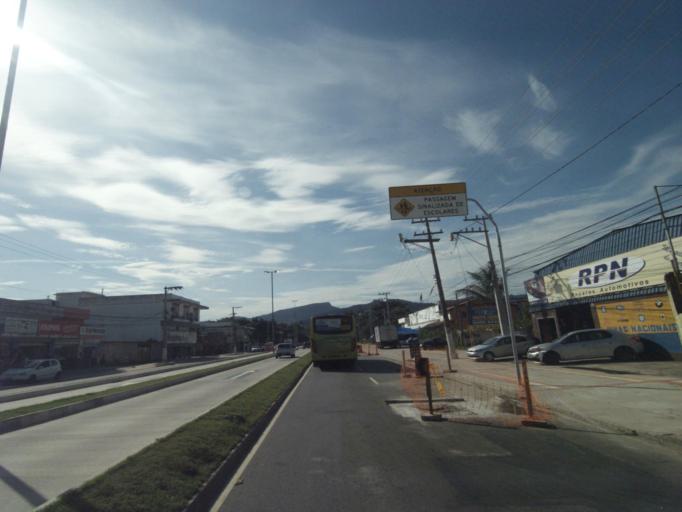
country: BR
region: Rio de Janeiro
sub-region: Niteroi
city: Niteroi
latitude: -22.9520
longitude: -43.0284
